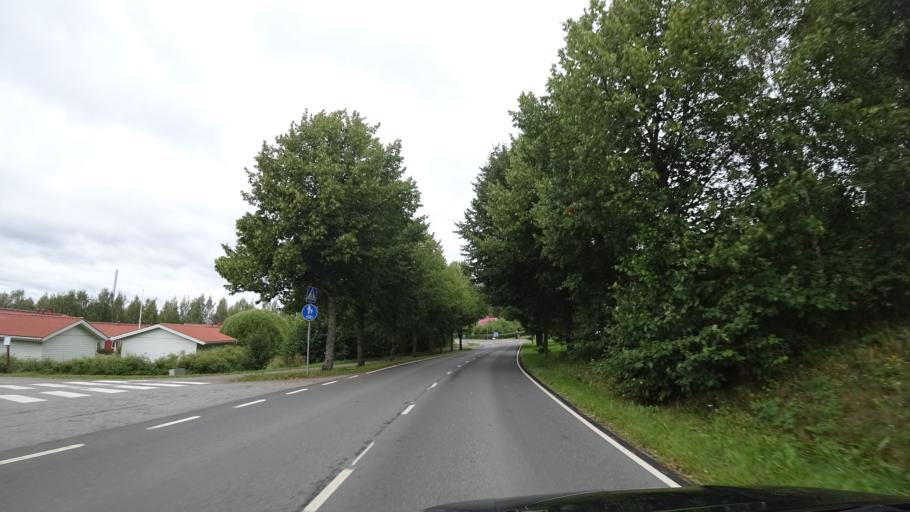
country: FI
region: Haeme
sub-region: Haemeenlinna
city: Lammi
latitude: 61.0869
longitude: 25.0040
